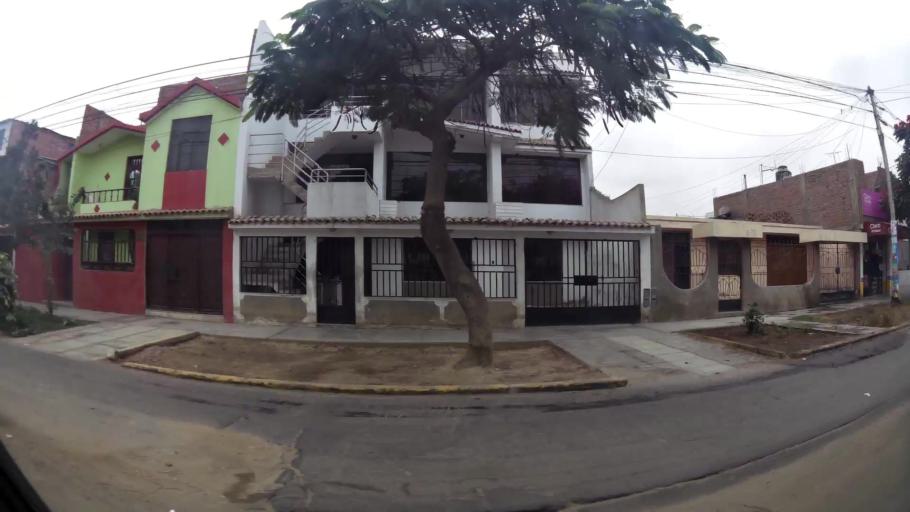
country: PE
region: La Libertad
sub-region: Provincia de Trujillo
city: Trujillo
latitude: -8.1124
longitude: -79.0407
